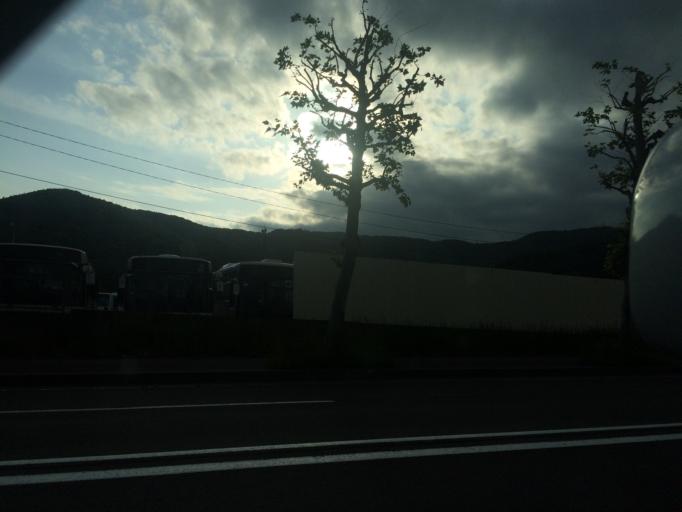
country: JP
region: Hokkaido
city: Sapporo
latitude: 43.0068
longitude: 141.3478
